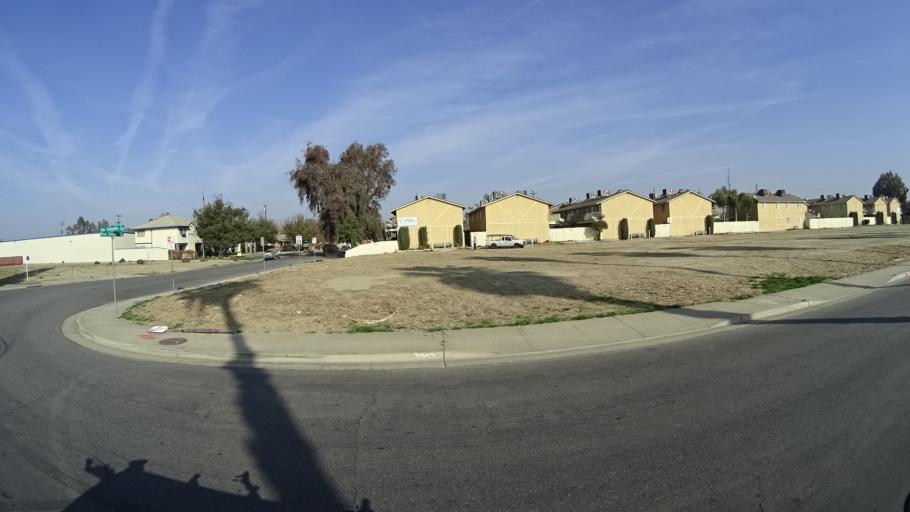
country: US
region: California
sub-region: Kern County
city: Bakersfield
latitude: 35.3185
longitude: -119.0344
